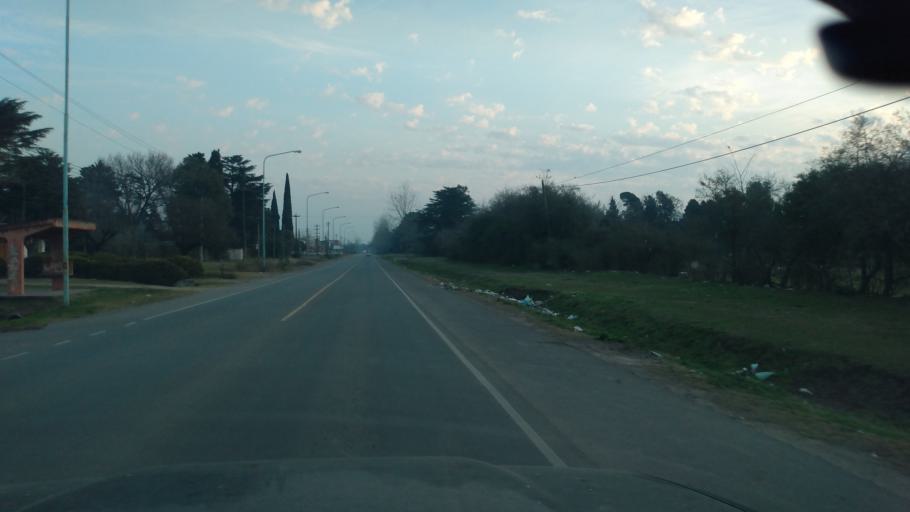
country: AR
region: Buenos Aires
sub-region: Partido de Lujan
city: Lujan
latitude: -34.5588
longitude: -59.1310
